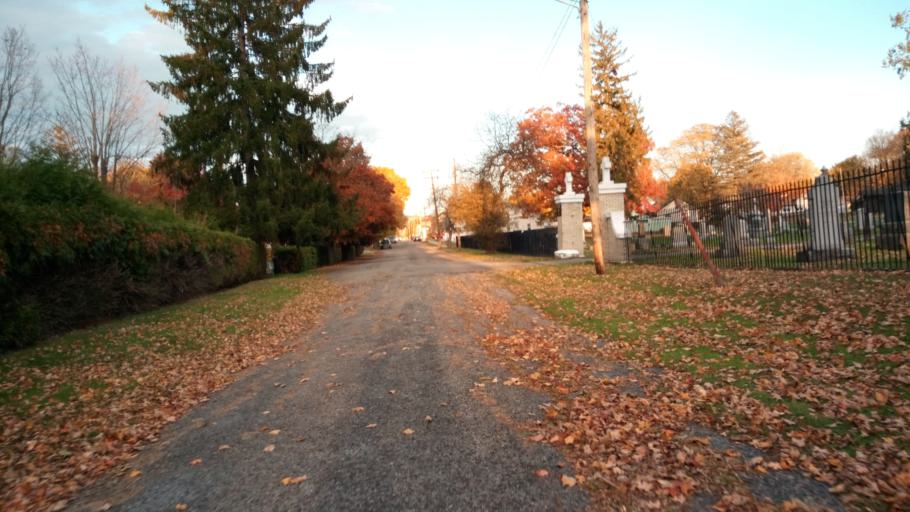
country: US
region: New York
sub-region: Chemung County
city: Elmira
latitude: 42.0736
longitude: -76.8165
